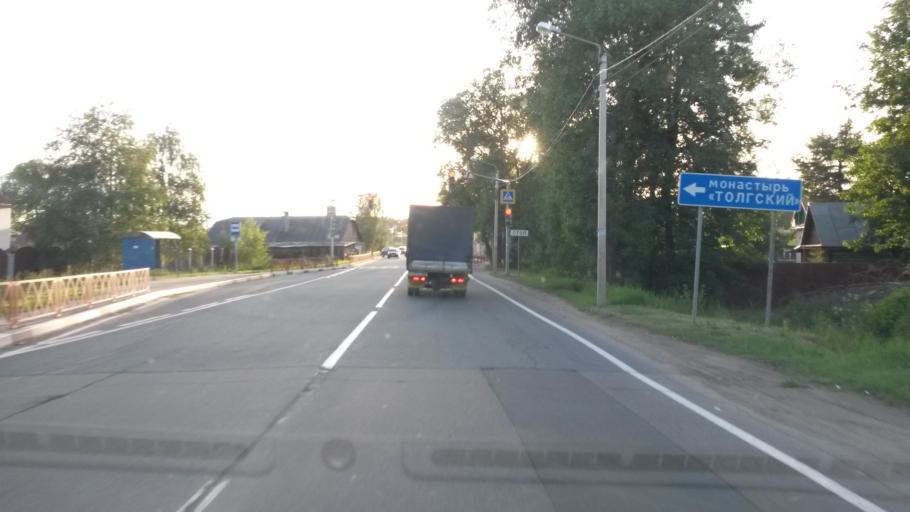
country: RU
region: Jaroslavl
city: Yaroslavl
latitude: 57.7110
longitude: 39.8380
